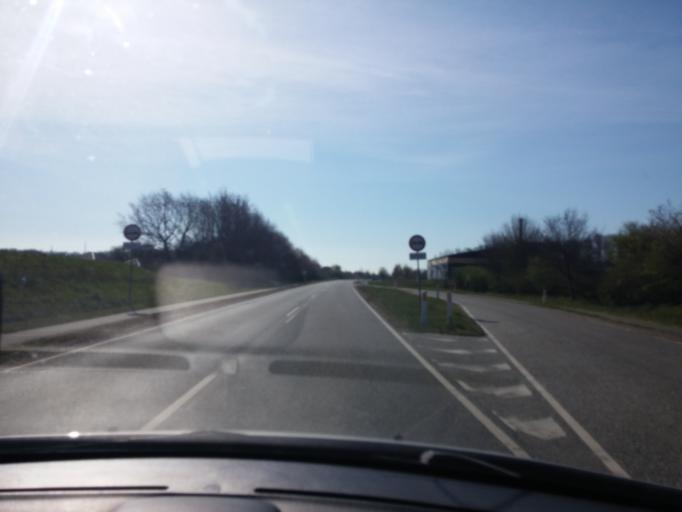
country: DK
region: Central Jutland
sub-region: Odder Kommune
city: Odder
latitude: 55.9257
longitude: 10.2426
